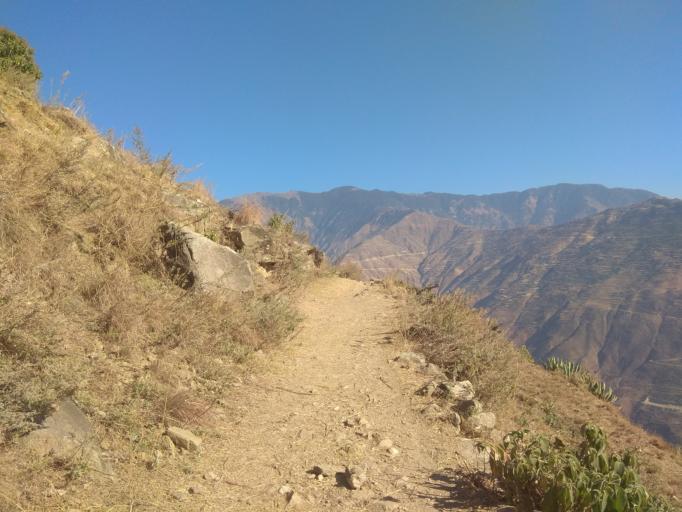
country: NP
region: Mid Western
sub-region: Karnali Zone
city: Jumla
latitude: 29.3157
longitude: 81.7412
